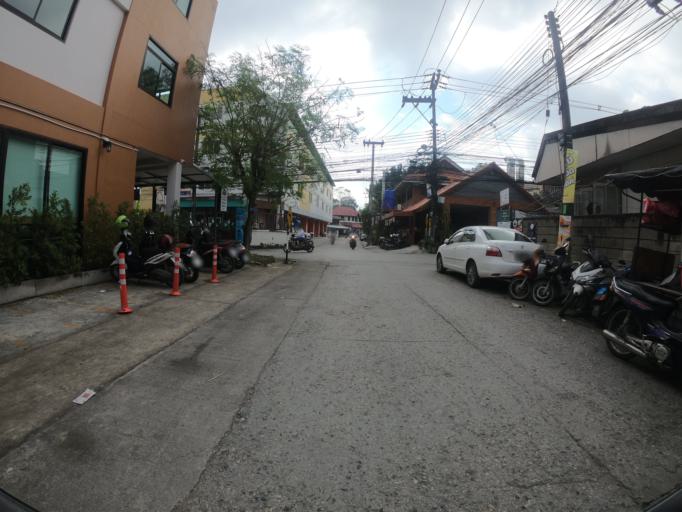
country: TH
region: Chiang Mai
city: Chiang Mai
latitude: 18.7922
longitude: 98.9516
